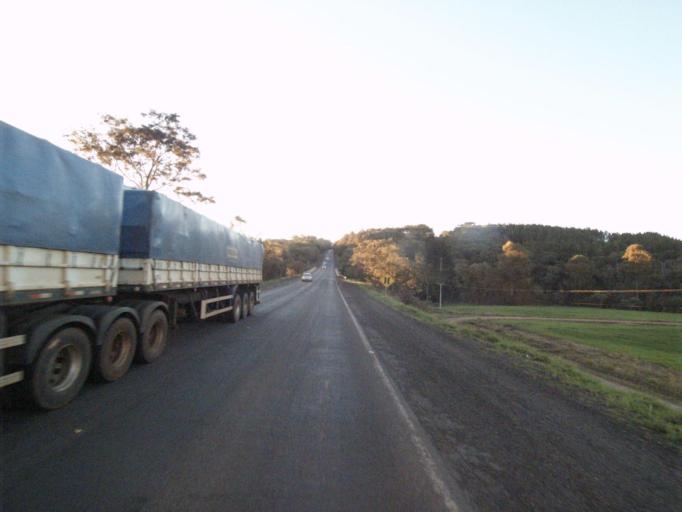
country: BR
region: Santa Catarina
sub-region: Sao Lourenco Do Oeste
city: Sao Lourenco dOeste
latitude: -26.7995
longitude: -53.1908
